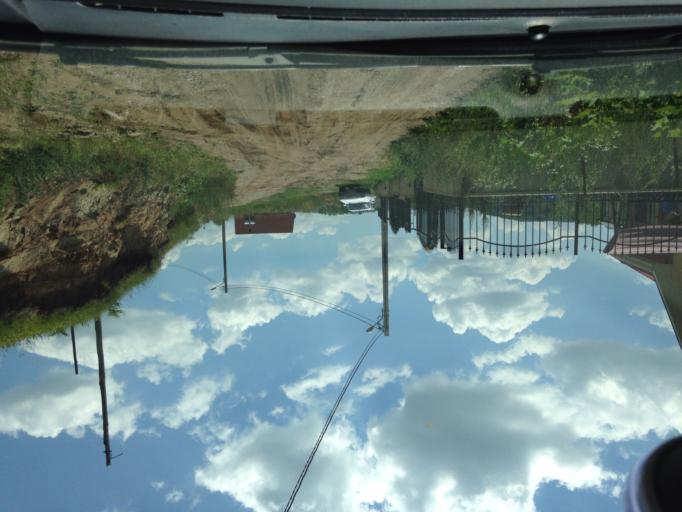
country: RO
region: Cluj
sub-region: Comuna Floresti
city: Floresti
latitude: 46.7404
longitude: 23.5326
